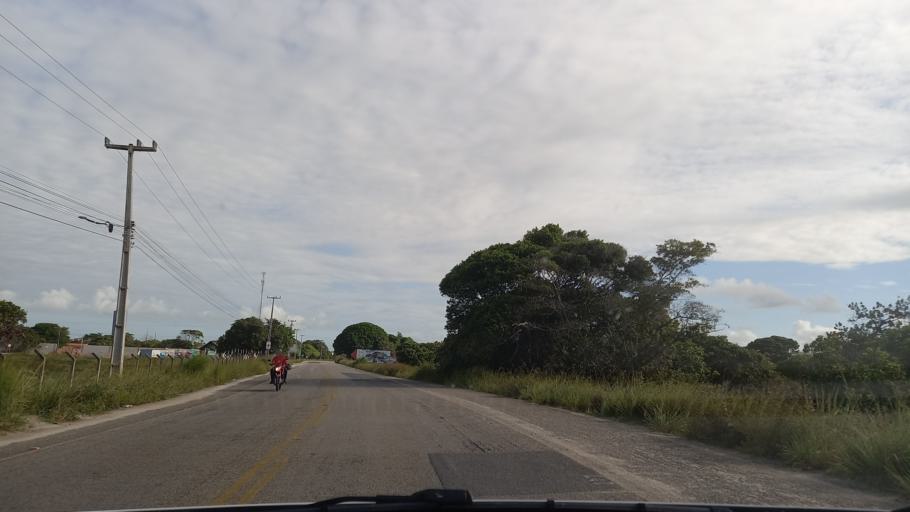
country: BR
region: Pernambuco
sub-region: Tamandare
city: Tamandare
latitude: -8.7162
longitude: -35.0939
